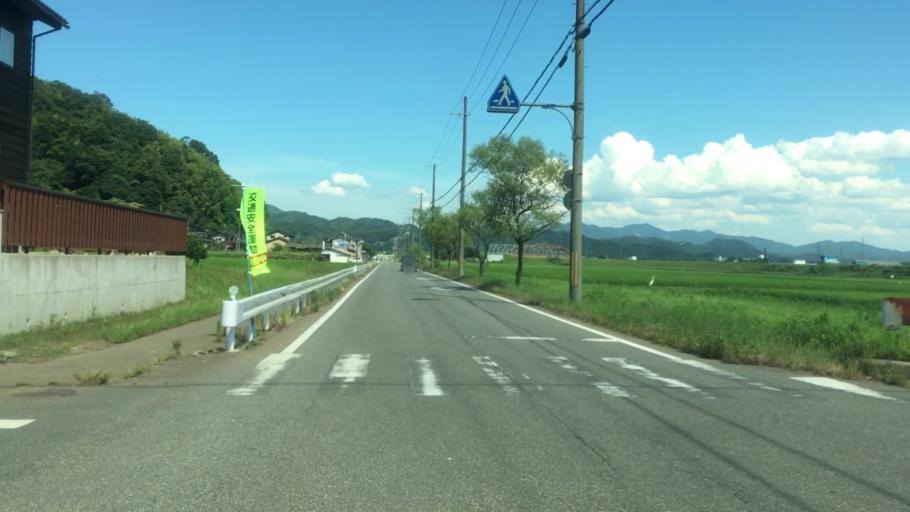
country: JP
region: Hyogo
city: Toyooka
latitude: 35.5667
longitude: 134.7958
